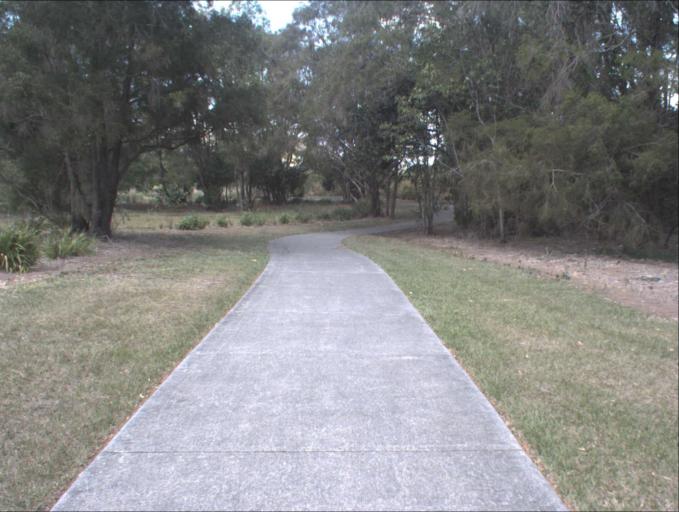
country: AU
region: Queensland
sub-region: Logan
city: Slacks Creek
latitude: -27.6713
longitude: 153.1587
